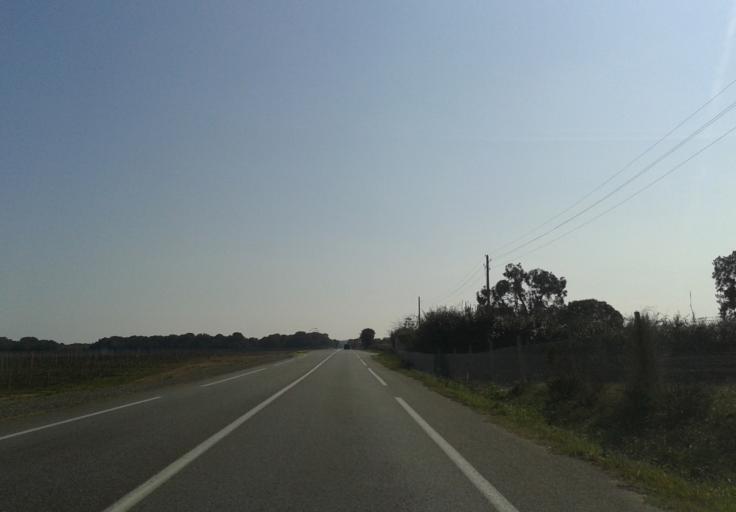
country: FR
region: Corsica
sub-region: Departement de la Haute-Corse
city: Cervione
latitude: 42.2810
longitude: 9.5504
